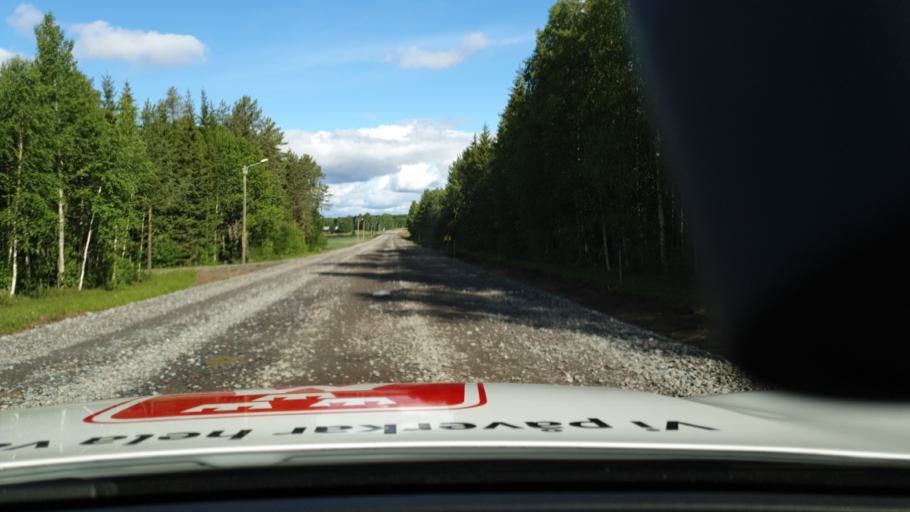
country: SE
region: Norrbotten
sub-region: Bodens Kommun
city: Boden
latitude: 65.8822
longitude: 21.4001
